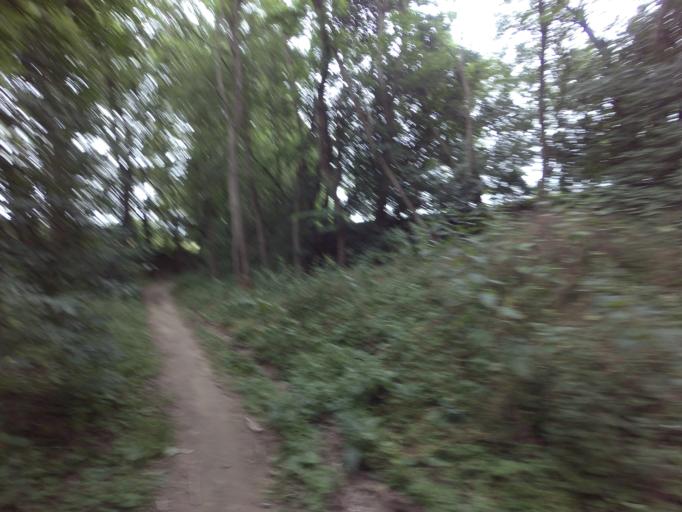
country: NL
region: Limburg
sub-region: Eijsden-Margraten
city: Margraten
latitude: 50.7891
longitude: 5.7804
